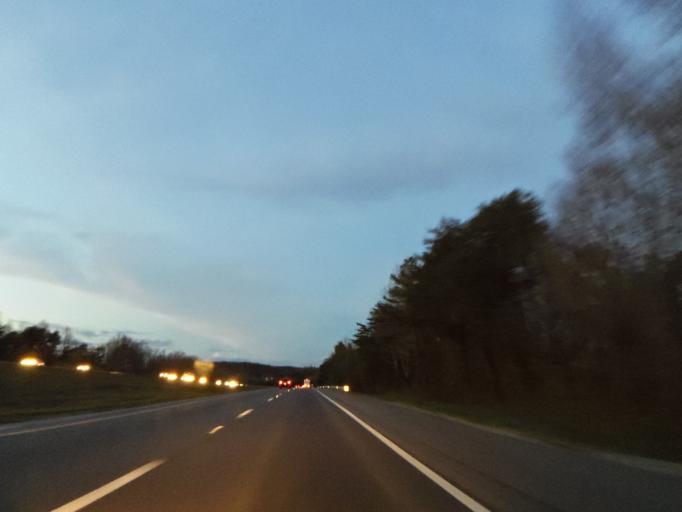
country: US
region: Kentucky
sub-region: Whitley County
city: Williamsburg
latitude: 36.8308
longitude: -84.1634
